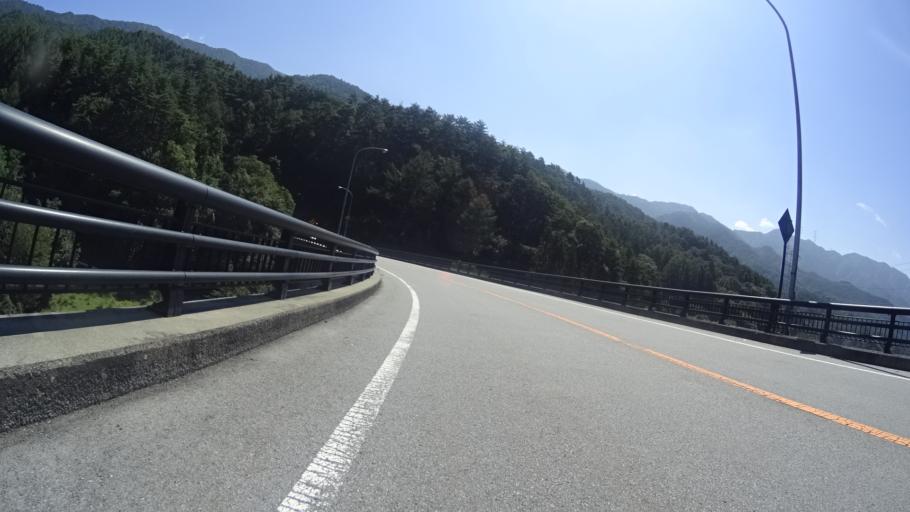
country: JP
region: Yamanashi
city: Enzan
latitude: 35.7485
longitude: 138.8067
